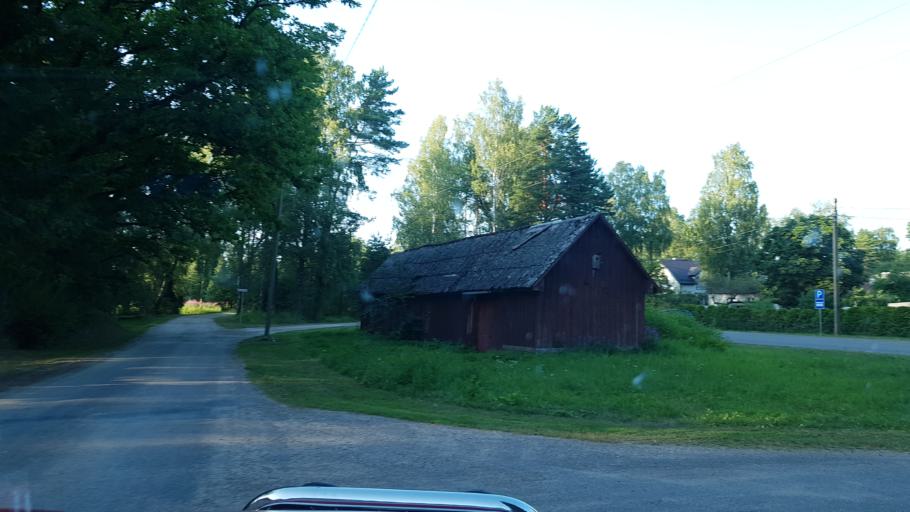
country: EE
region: Harju
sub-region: Saku vald
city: Saku
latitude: 59.2382
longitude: 24.6861
